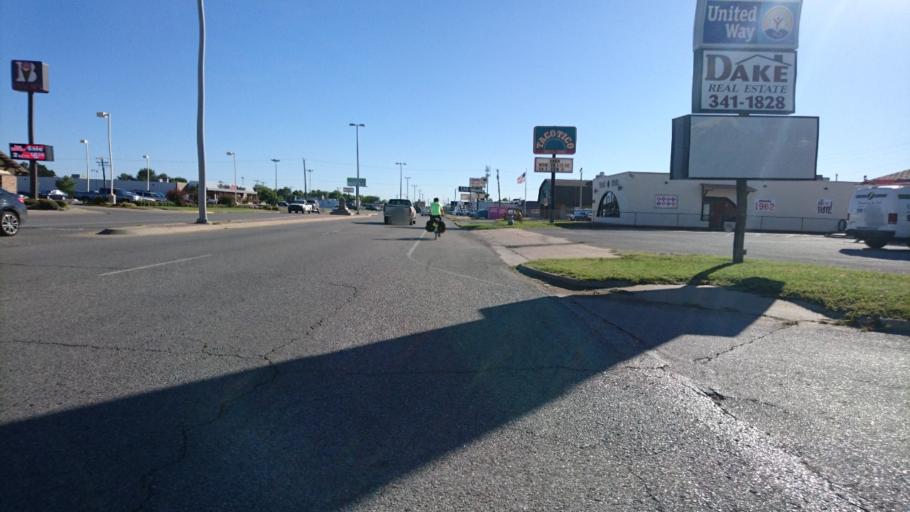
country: US
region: Oklahoma
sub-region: Rogers County
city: Claremore
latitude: 36.3210
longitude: -95.6109
